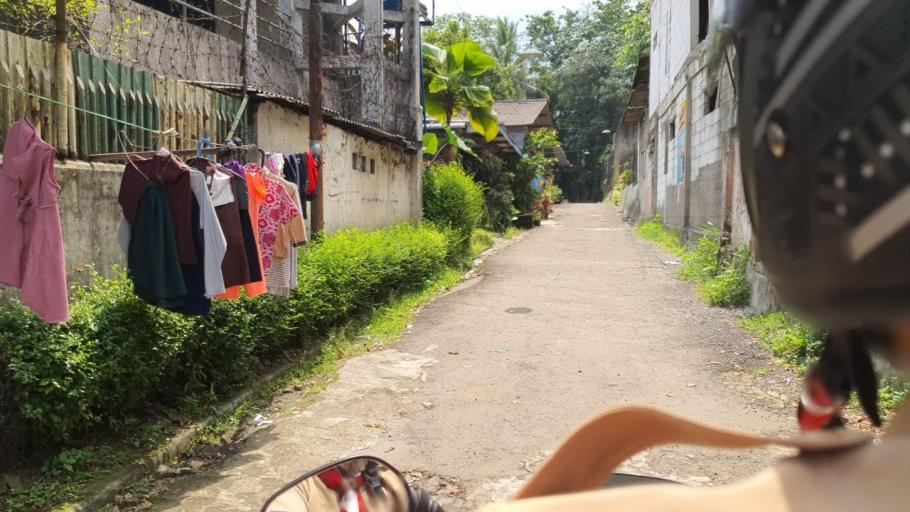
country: ID
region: West Java
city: Caringin
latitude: -6.6537
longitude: 106.8762
